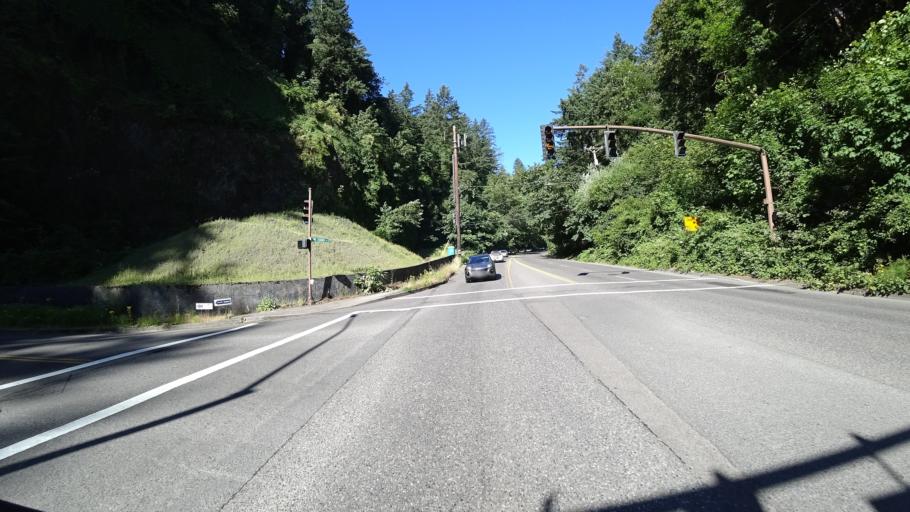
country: US
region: Oregon
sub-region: Multnomah County
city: Portland
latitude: 45.5230
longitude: -122.7112
